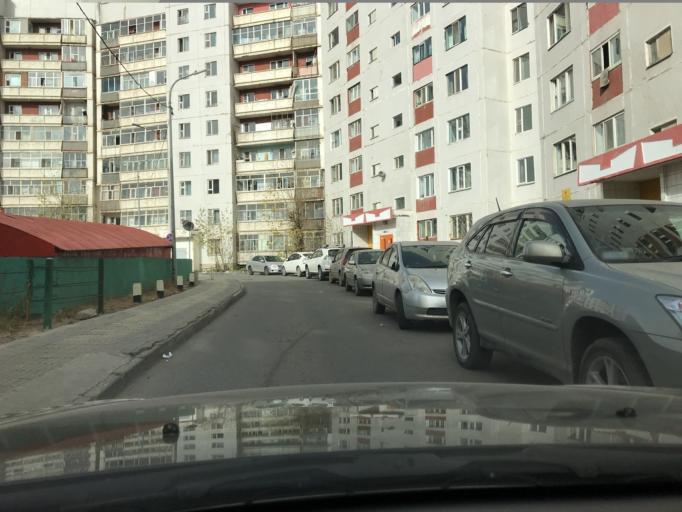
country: MN
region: Ulaanbaatar
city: Ulaanbaatar
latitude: 47.9176
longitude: 106.9411
